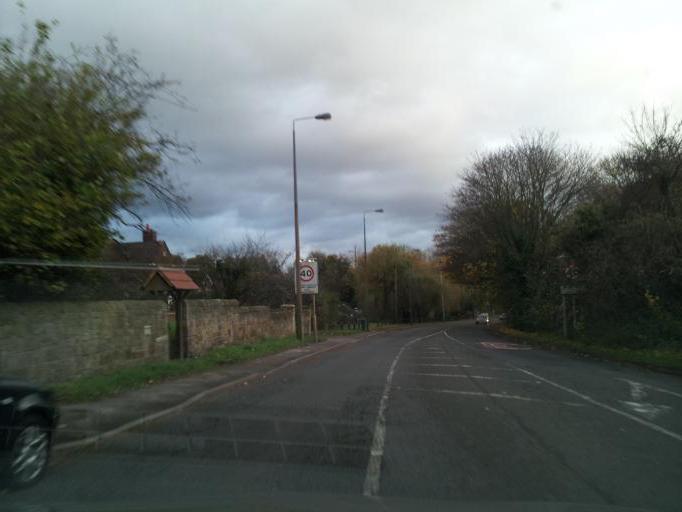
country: GB
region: England
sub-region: Nottinghamshire
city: Kimberley
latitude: 52.9557
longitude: -1.2773
